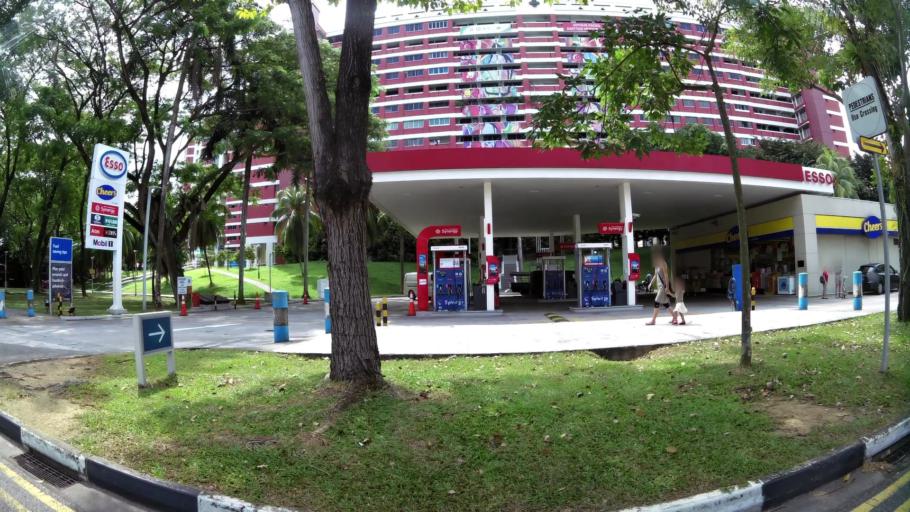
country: SG
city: Singapore
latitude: 1.3401
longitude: 103.7748
